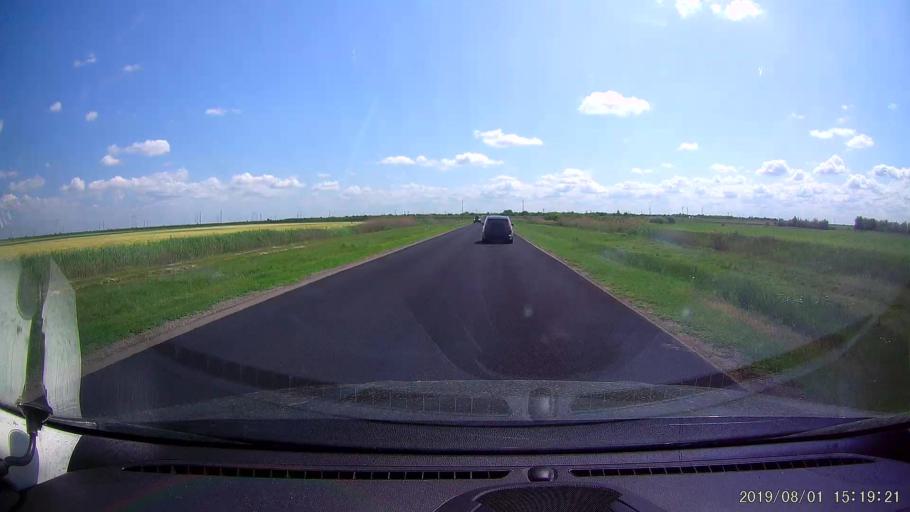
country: RO
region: Braila
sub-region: Comuna Unirea
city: Unirea
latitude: 45.0907
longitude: 27.8133
